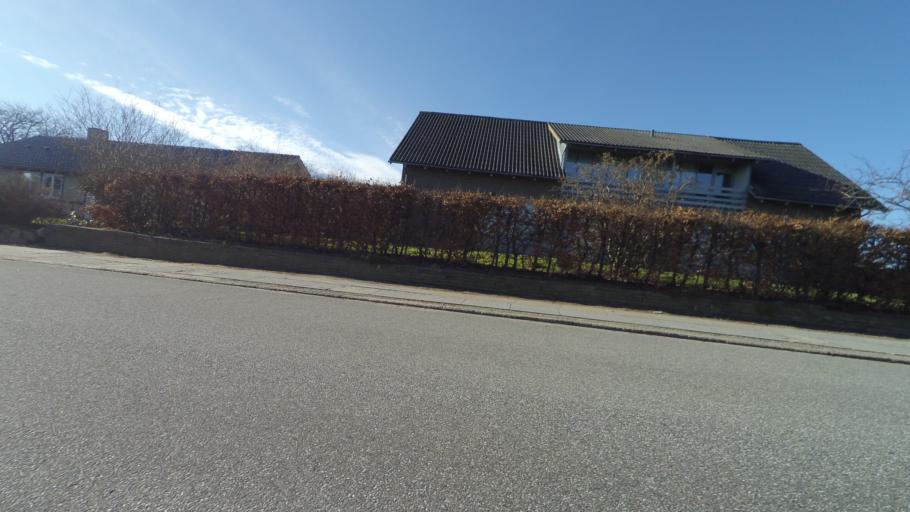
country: DK
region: Central Jutland
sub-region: Arhus Kommune
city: Tranbjerg
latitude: 56.1071
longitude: 10.0990
